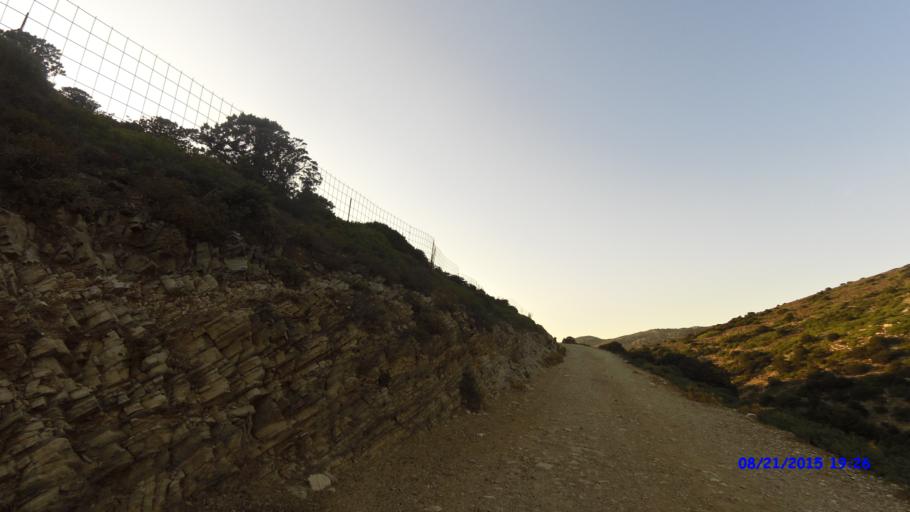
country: GR
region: South Aegean
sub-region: Nomos Kykladon
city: Antiparos
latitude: 36.9866
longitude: 25.0294
